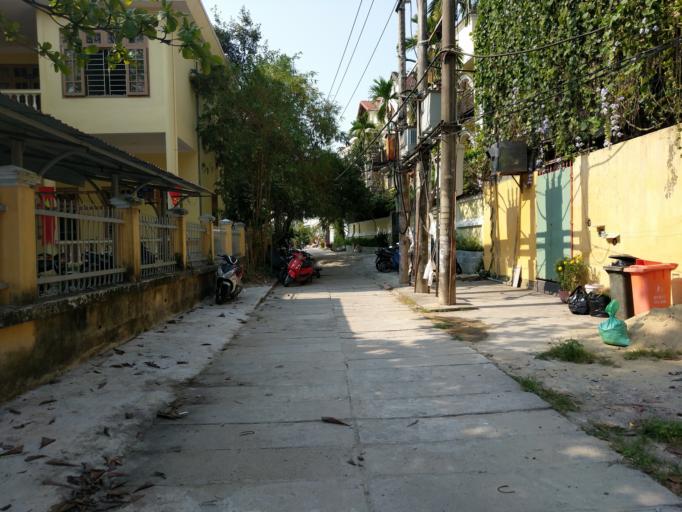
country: VN
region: Quang Nam
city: Hoi An
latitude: 15.8804
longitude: 108.3258
